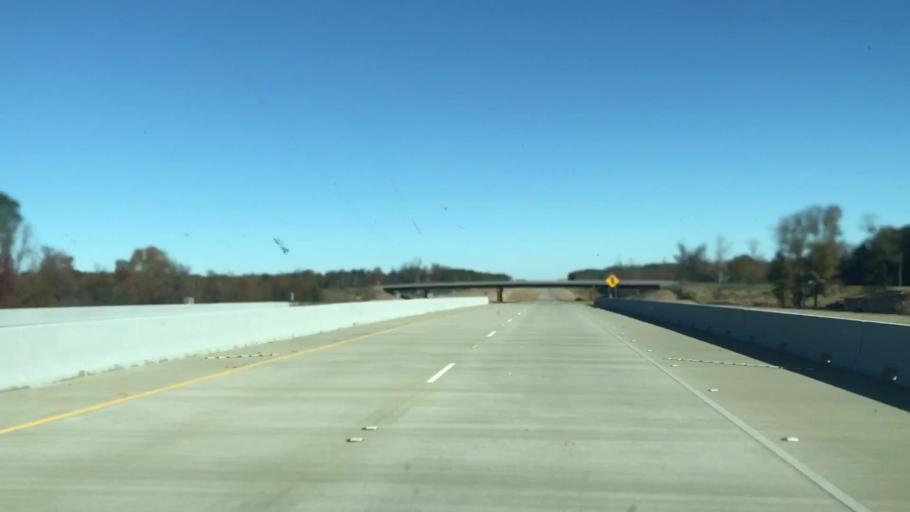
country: US
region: Louisiana
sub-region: Caddo Parish
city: Blanchard
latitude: 32.5972
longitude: -93.8319
